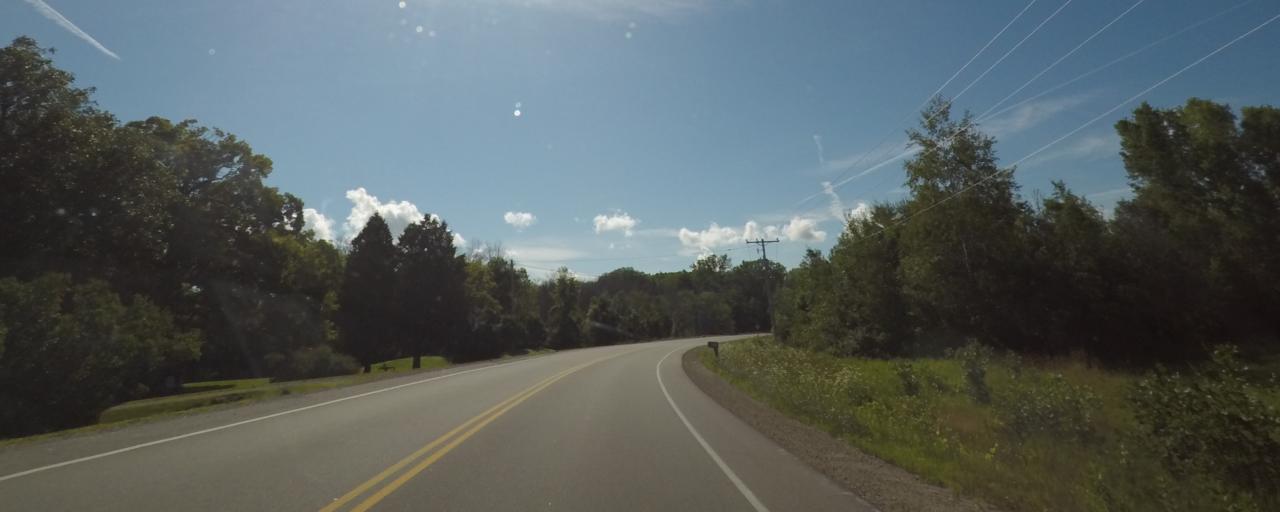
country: US
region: Wisconsin
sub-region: Jefferson County
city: Ixonia
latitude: 43.0732
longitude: -88.6381
